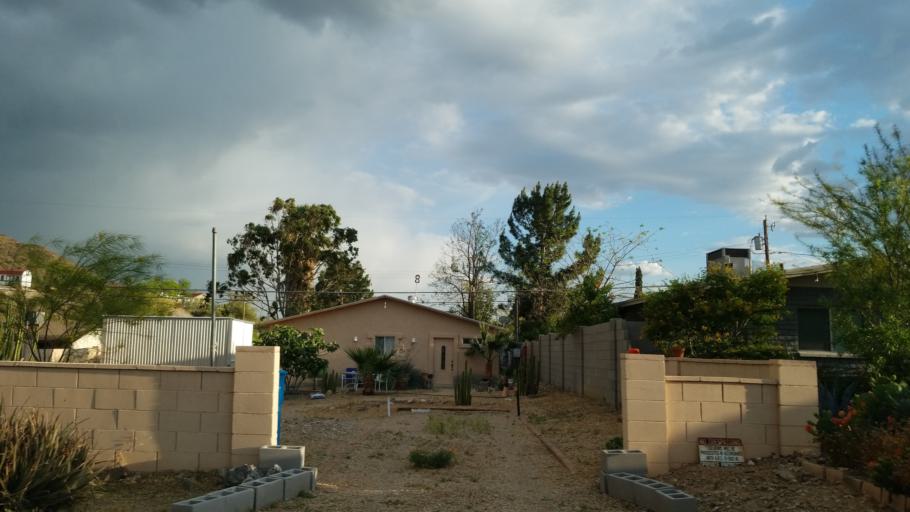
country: US
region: Arizona
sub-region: Maricopa County
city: Paradise Valley
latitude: 33.5911
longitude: -112.0504
